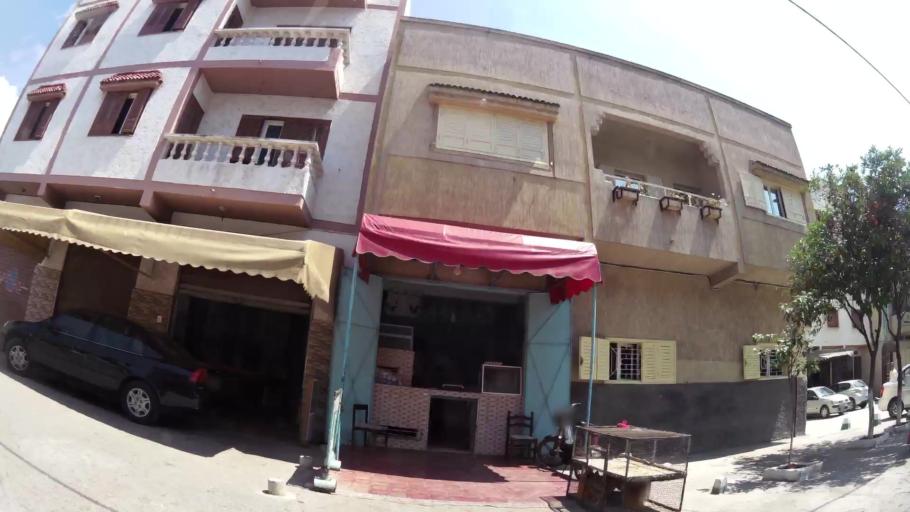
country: MA
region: Rabat-Sale-Zemmour-Zaer
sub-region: Skhirate-Temara
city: Temara
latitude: 33.9694
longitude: -6.8892
